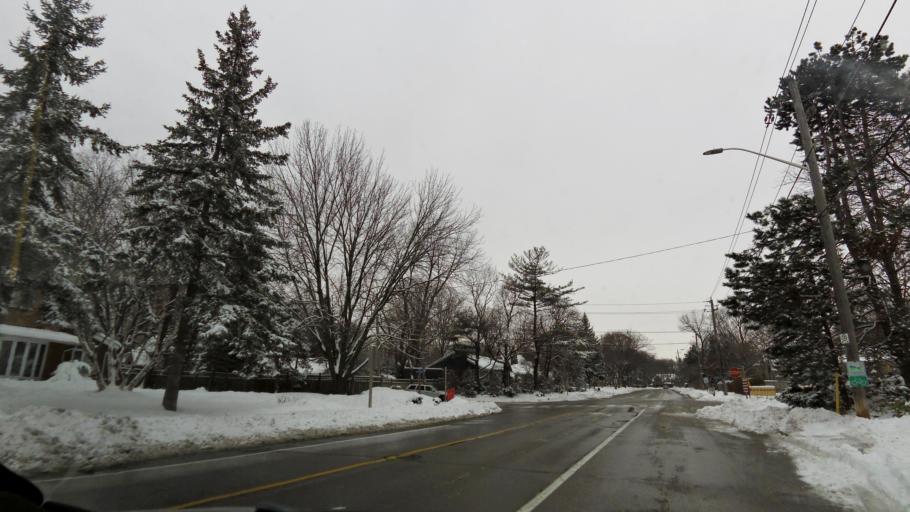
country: CA
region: Ontario
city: Mississauga
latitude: 43.5365
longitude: -79.6280
